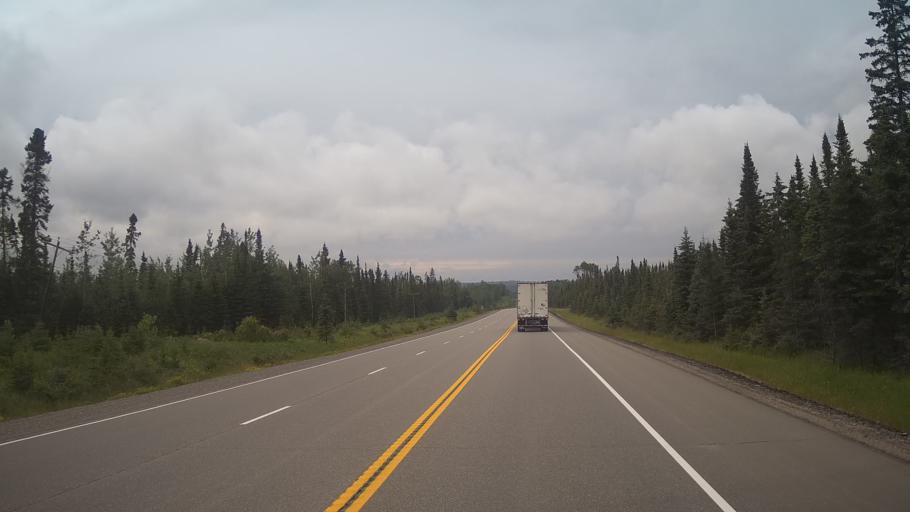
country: CA
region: Ontario
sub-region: Thunder Bay District
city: Thunder Bay
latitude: 48.7093
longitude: -89.8881
